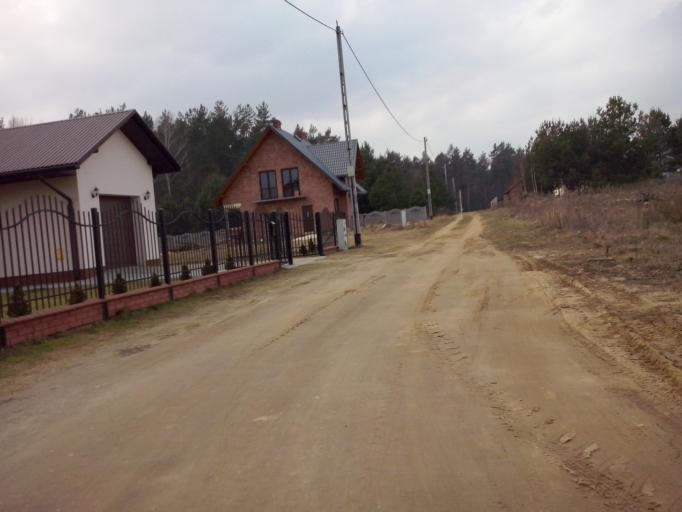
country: PL
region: Subcarpathian Voivodeship
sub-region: Powiat nizanski
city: Krzeszow
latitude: 50.4134
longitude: 22.3425
